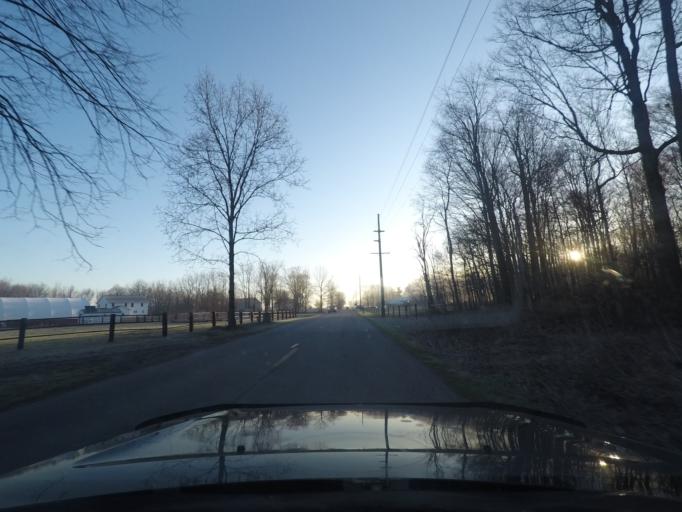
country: US
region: Indiana
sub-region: Marshall County
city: Bremen
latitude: 41.4572
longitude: -86.0876
